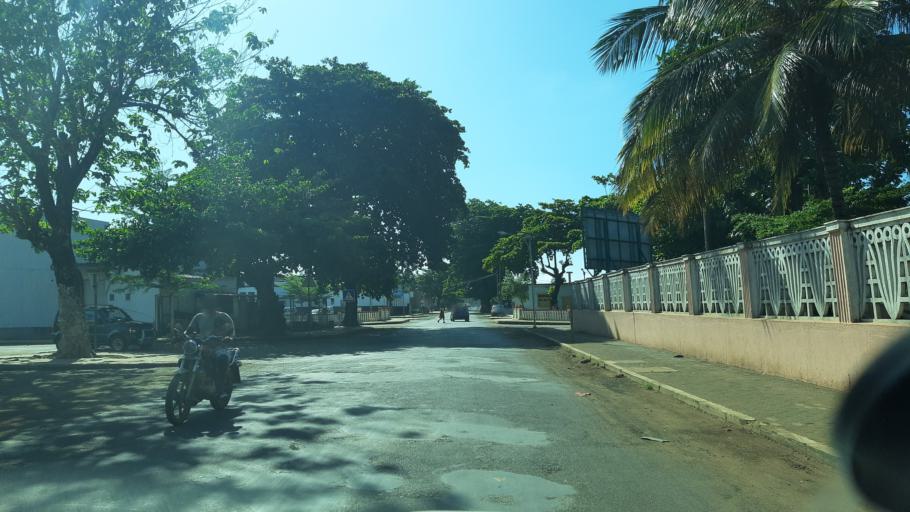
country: ST
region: Sao Tome Island
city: Sao Tome
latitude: 0.3368
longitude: 6.7310
